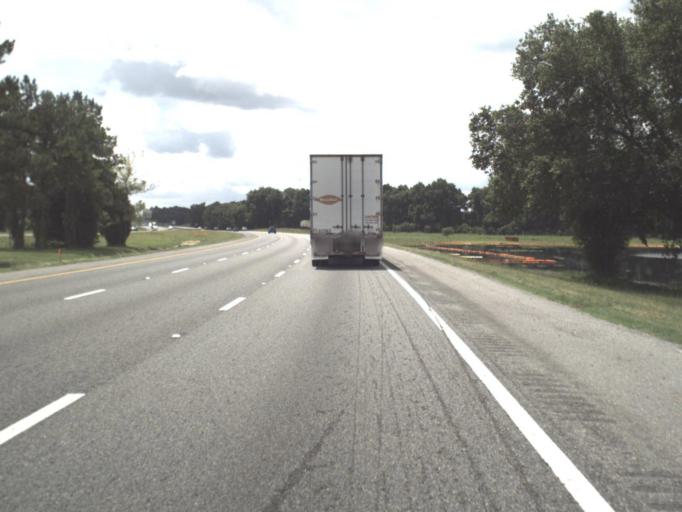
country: US
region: Florida
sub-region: Suwannee County
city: Wellborn
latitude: 30.2404
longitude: -82.7394
